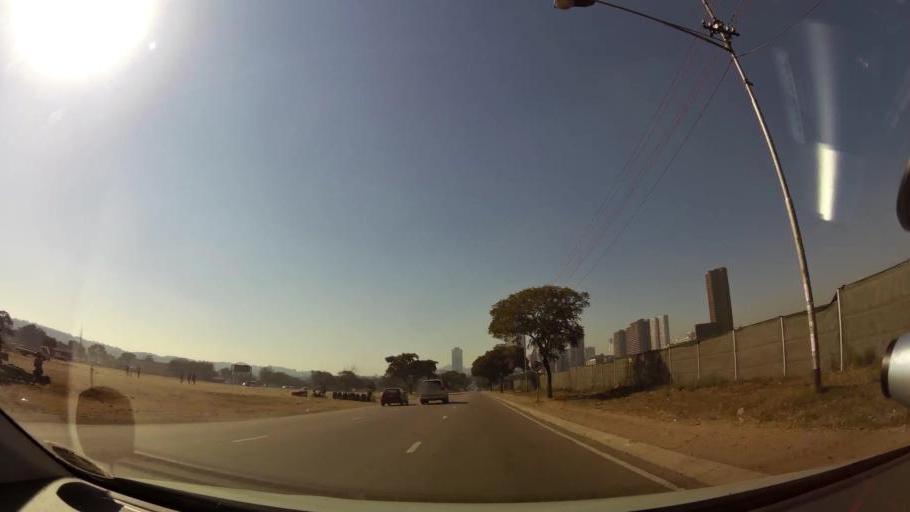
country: ZA
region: Gauteng
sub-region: City of Tshwane Metropolitan Municipality
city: Pretoria
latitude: -25.7430
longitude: 28.1741
